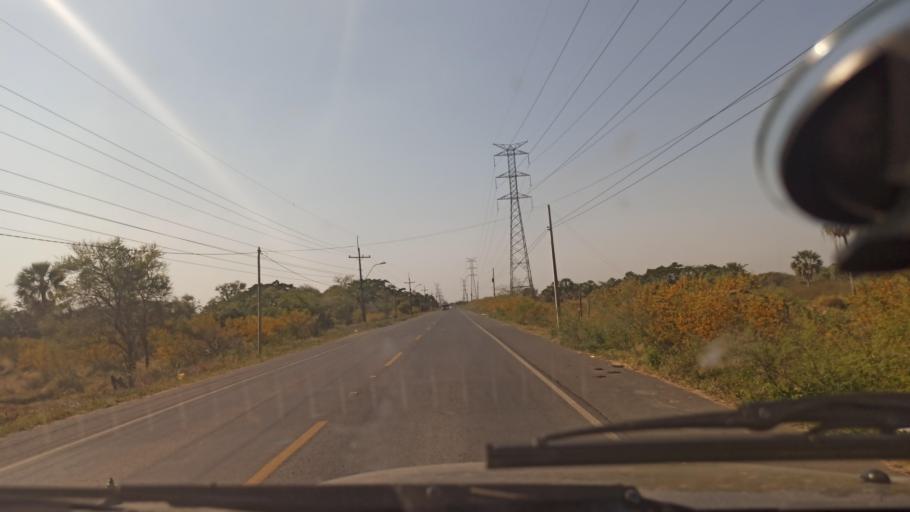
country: PY
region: Presidente Hayes
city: Nanawa
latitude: -25.2508
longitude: -57.6713
